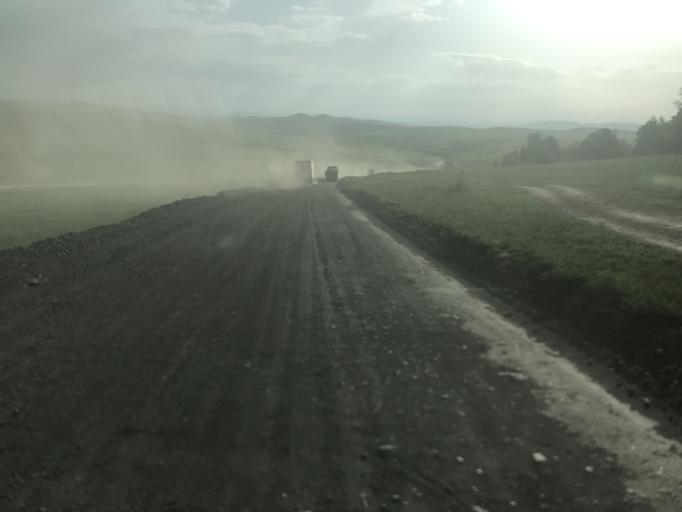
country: MN
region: Central Aimak
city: Javhlant
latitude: 48.6486
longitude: 106.0950
